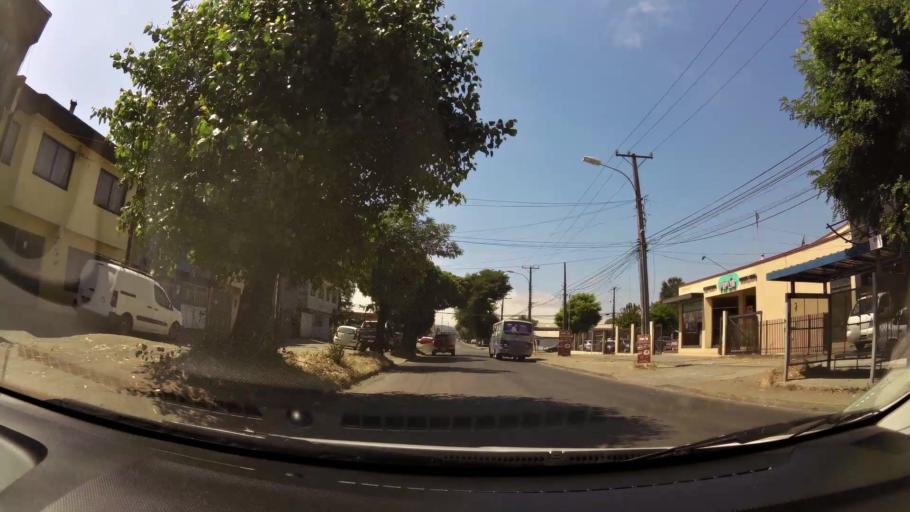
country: CL
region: Biobio
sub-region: Provincia de Concepcion
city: Concepcion
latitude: -36.8094
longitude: -73.0501
